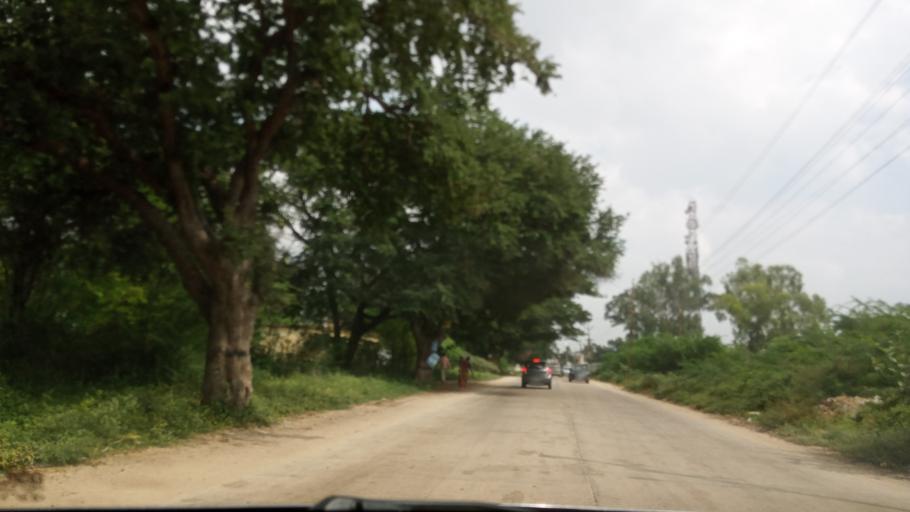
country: IN
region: Andhra Pradesh
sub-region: Chittoor
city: Madanapalle
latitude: 13.6349
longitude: 78.6255
